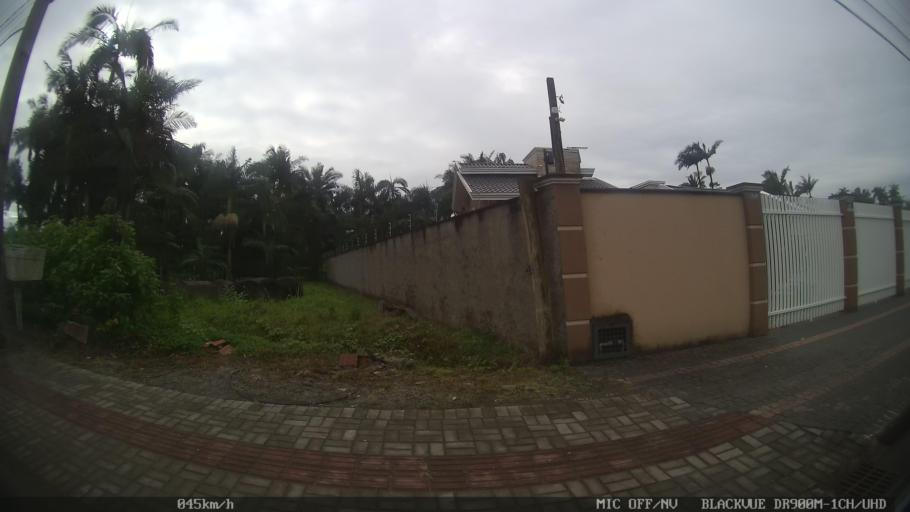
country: BR
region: Santa Catarina
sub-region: Joinville
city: Joinville
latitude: -26.0496
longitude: -48.8568
